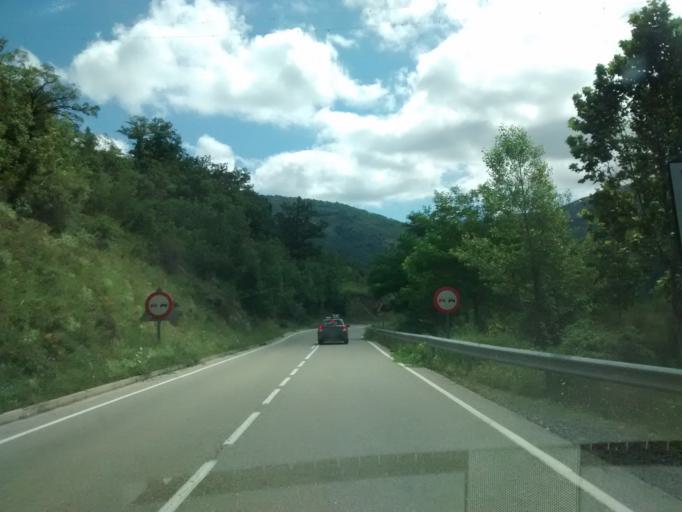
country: ES
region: La Rioja
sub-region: Provincia de La Rioja
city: Soto en Cameros
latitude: 42.3068
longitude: -2.4183
